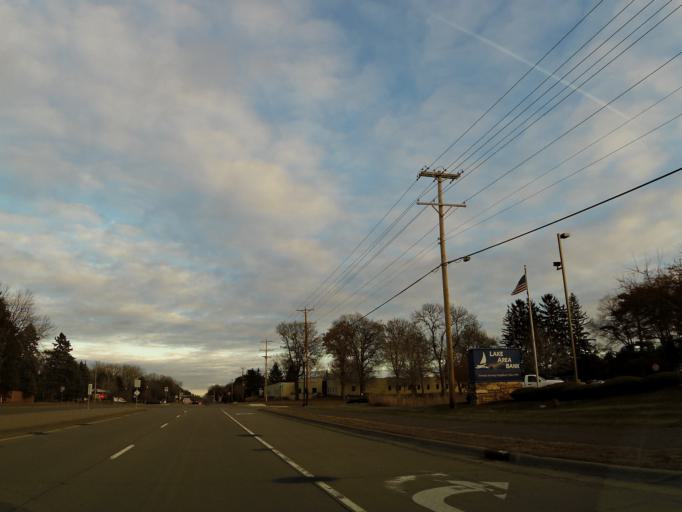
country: US
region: Minnesota
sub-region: Ramsey County
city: White Bear Lake
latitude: 45.0791
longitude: -93.0421
